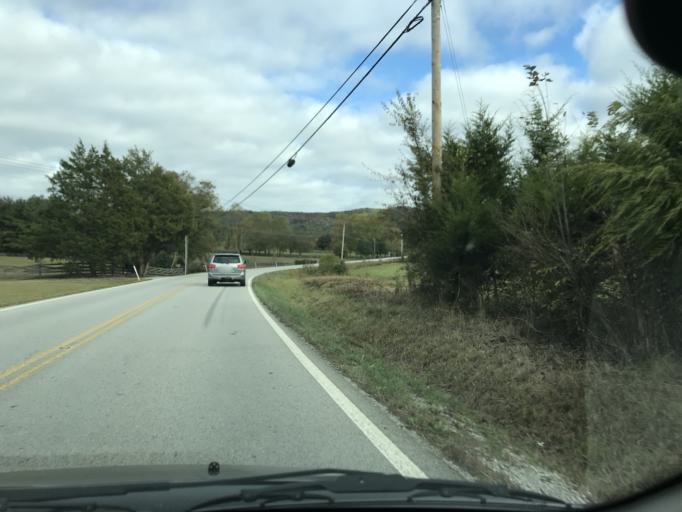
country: US
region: Tennessee
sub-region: Hamilton County
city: Lakesite
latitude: 35.1773
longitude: -85.0359
